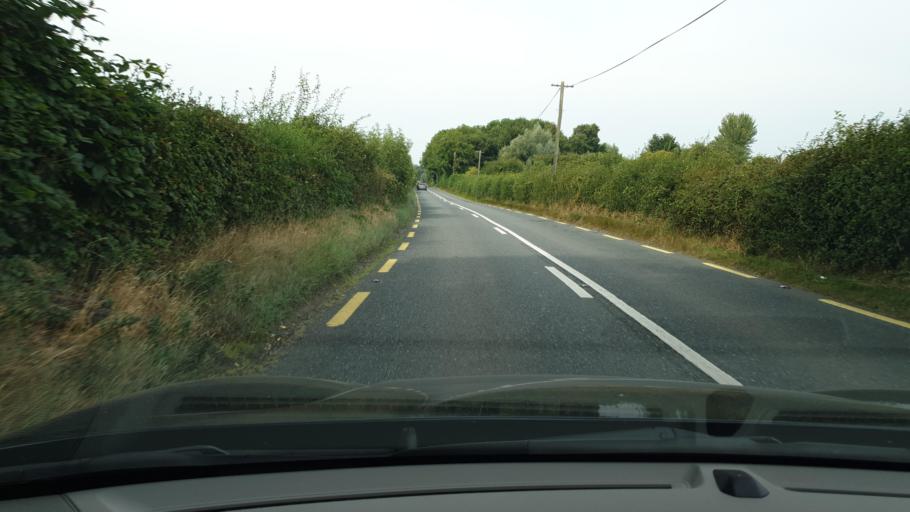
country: IE
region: Leinster
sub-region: An Mhi
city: Newtown Trim
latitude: 53.6294
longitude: -6.7759
